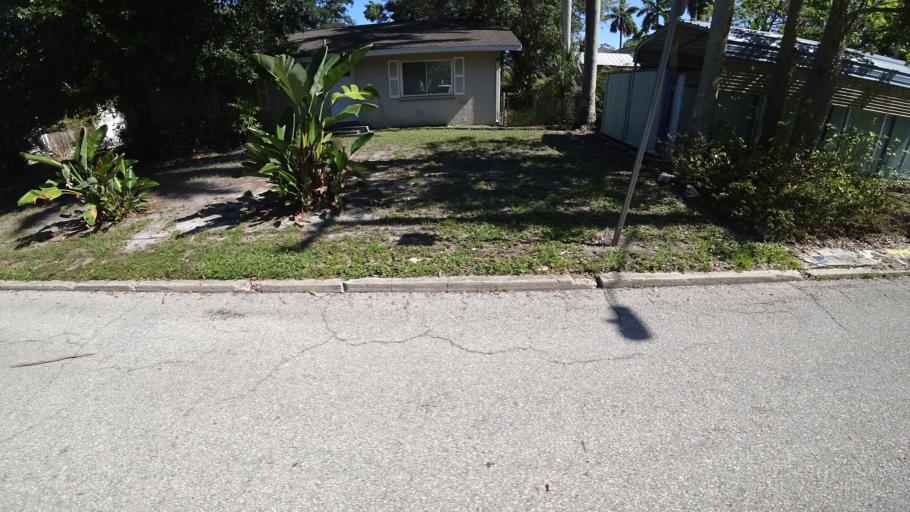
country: US
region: Florida
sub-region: Manatee County
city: Bradenton
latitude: 27.4992
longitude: -82.5878
